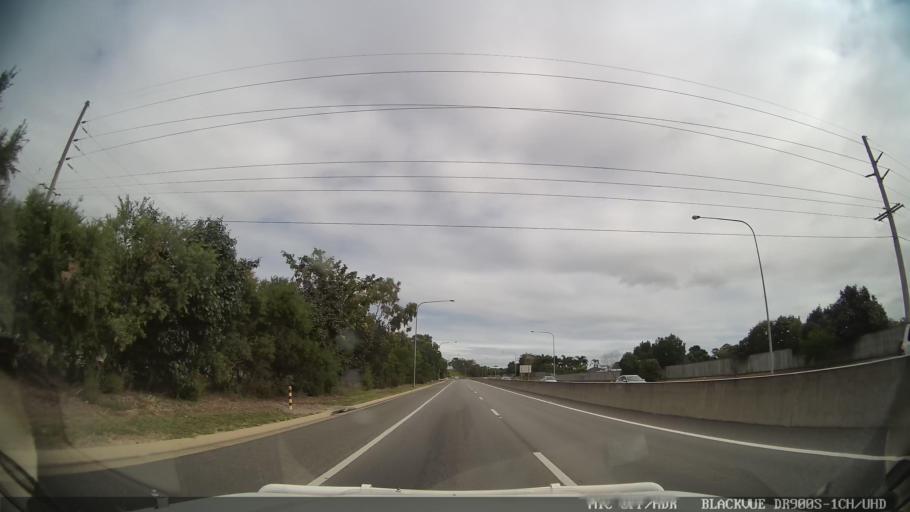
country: AU
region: Queensland
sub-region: Townsville
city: Bohle Plains
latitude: -19.3213
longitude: 146.7469
